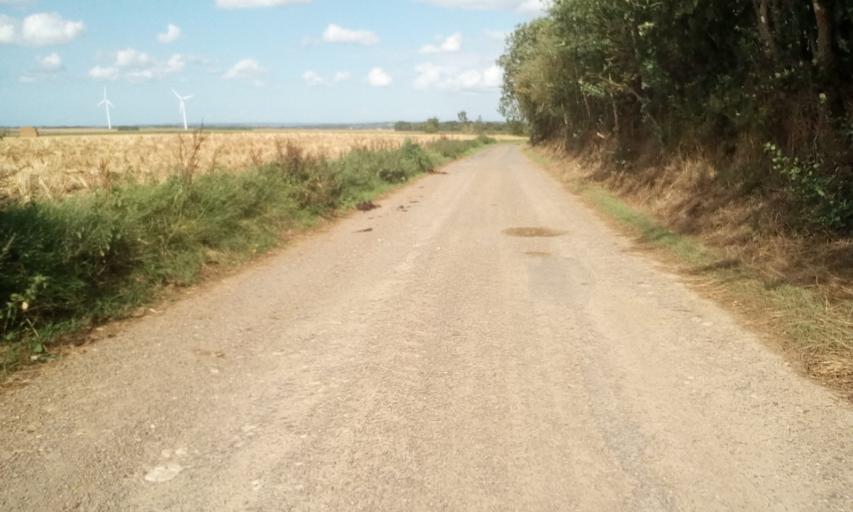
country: FR
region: Lower Normandy
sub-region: Departement du Calvados
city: Saint-Sylvain
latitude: 49.0768
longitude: -0.2371
